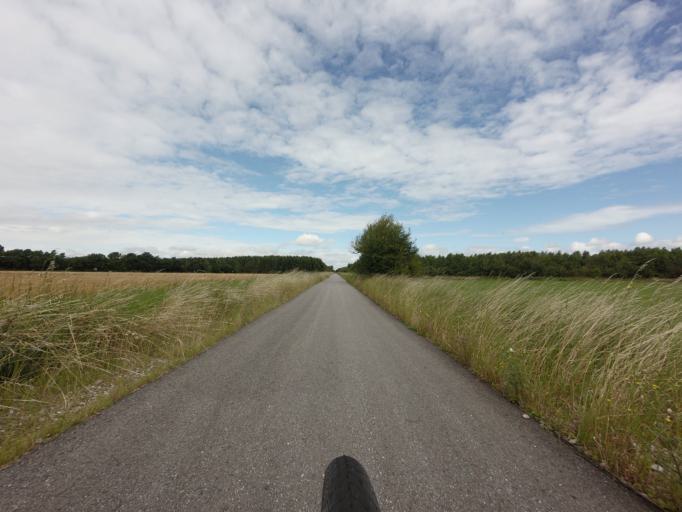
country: DK
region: Central Jutland
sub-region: Norddjurs Kommune
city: Auning
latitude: 56.4124
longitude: 10.3925
